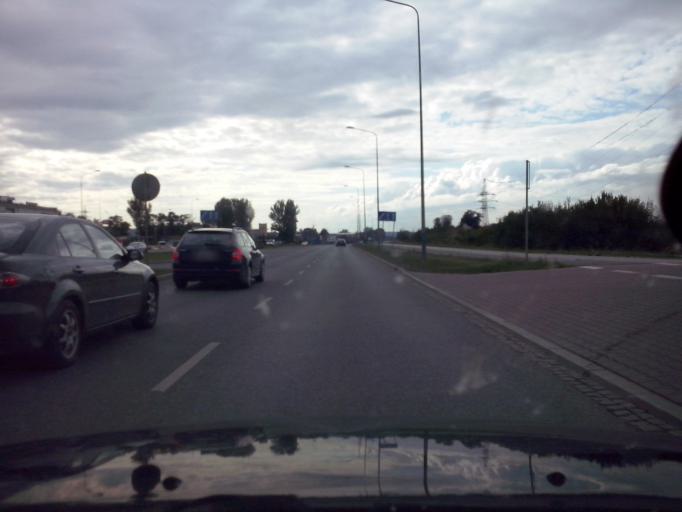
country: PL
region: Lesser Poland Voivodeship
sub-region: Powiat wielicki
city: Czarnochowice
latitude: 50.0380
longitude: 20.0161
